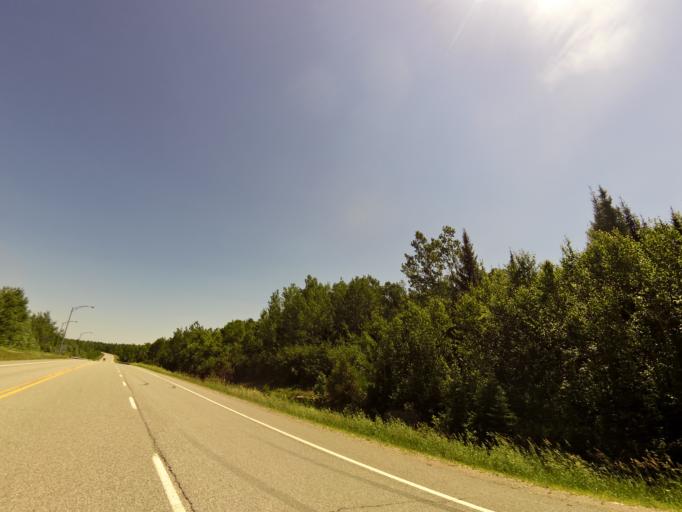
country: CA
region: Quebec
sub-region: Abitibi-Temiscamingue
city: Temiscaming
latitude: 46.7211
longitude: -79.0747
